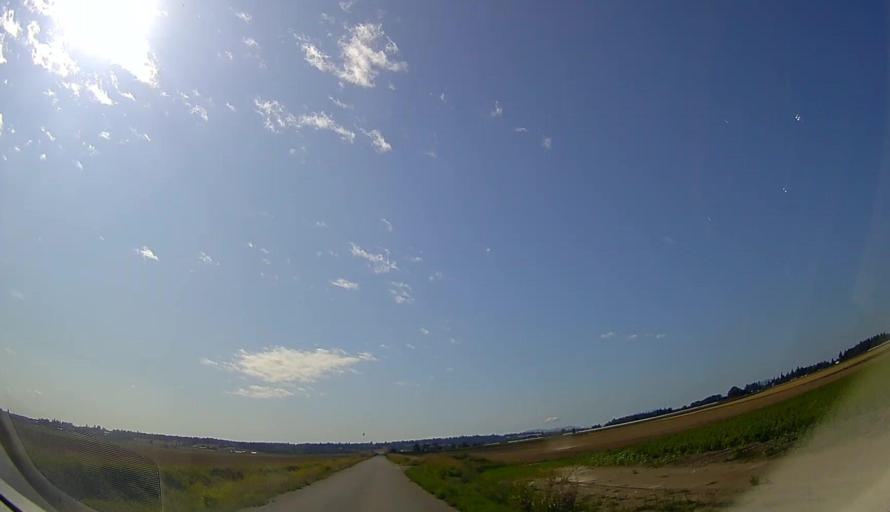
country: US
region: Washington
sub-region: Skagit County
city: Burlington
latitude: 48.4938
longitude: -122.3669
